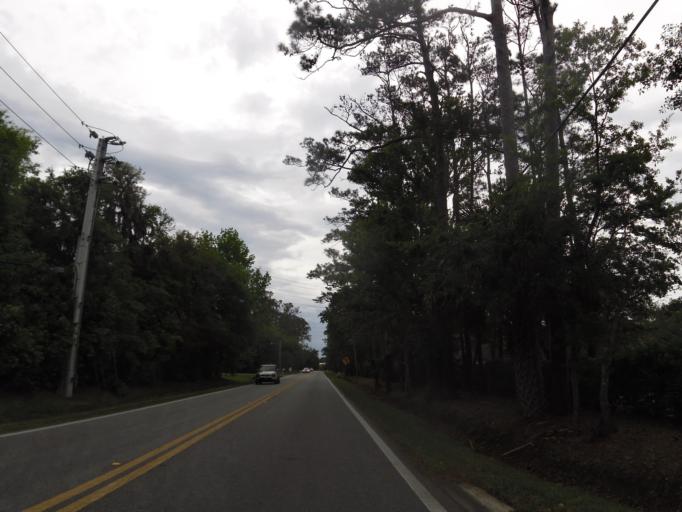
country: US
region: Florida
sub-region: Saint Johns County
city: Palm Valley
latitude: 30.1873
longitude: -81.3858
